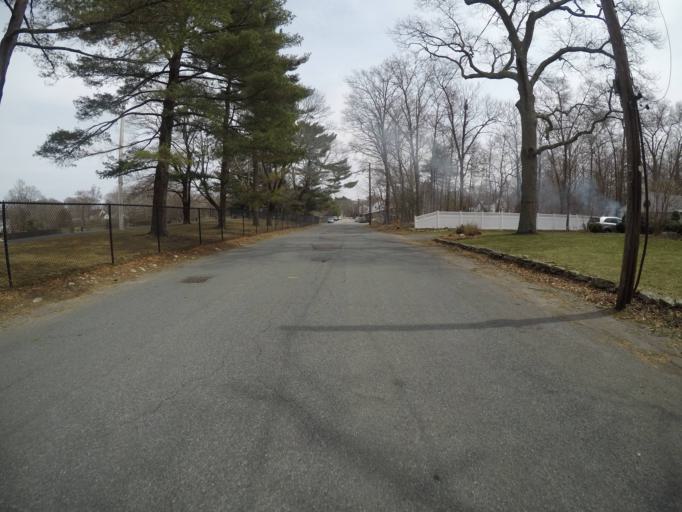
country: US
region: Massachusetts
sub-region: Bristol County
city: Easton
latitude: 42.0617
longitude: -71.1058
